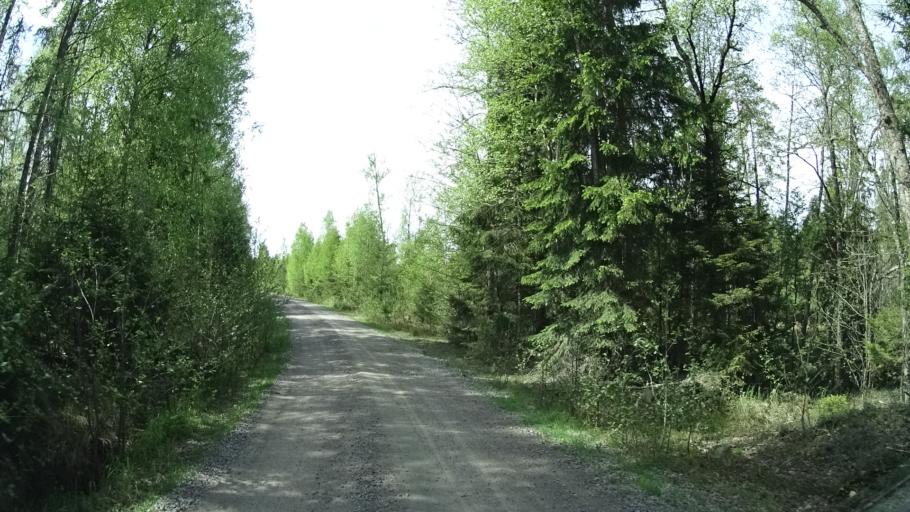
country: SE
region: OEstergoetland
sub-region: Finspangs Kommun
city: Finspang
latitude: 58.7790
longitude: 15.8455
